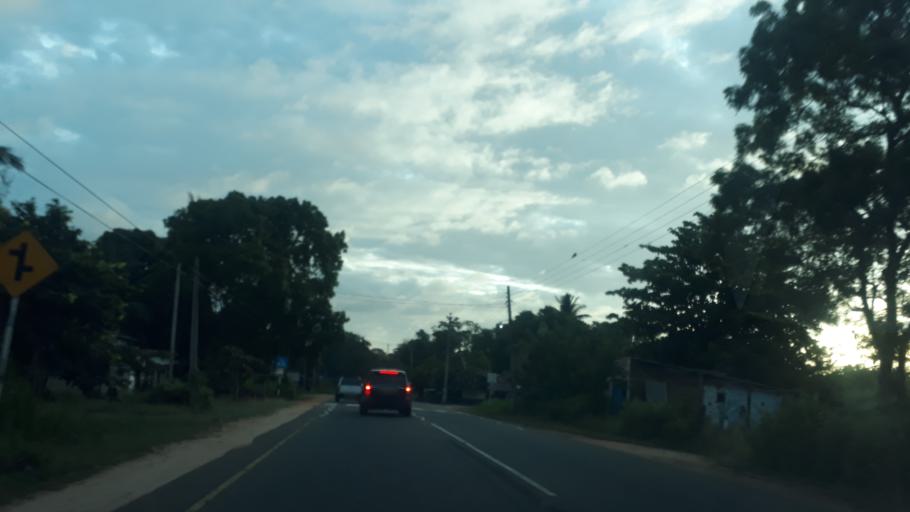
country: LK
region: Central
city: Sigiriya
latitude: 7.9773
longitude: 80.7158
